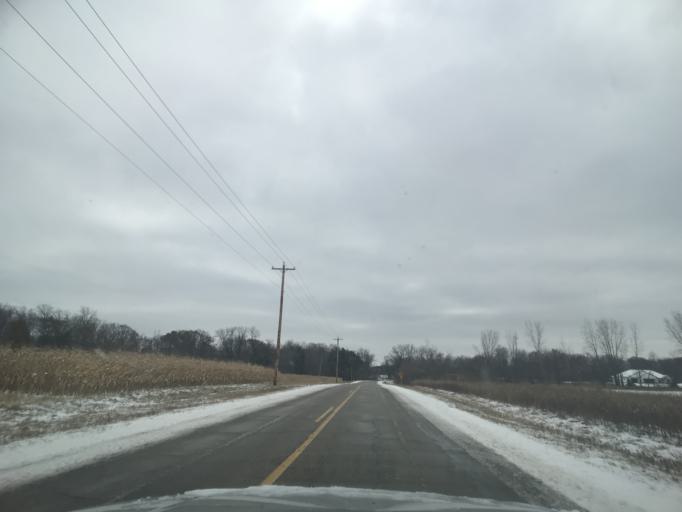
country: US
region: Wisconsin
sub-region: Brown County
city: Suamico
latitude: 44.7134
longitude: -88.0710
